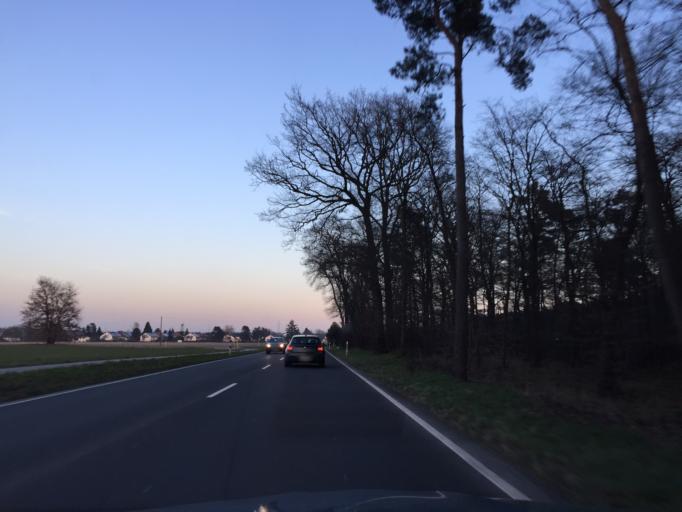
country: DE
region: Baden-Wuerttemberg
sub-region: Karlsruhe Region
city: Reilingen
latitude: 49.2876
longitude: 8.5482
